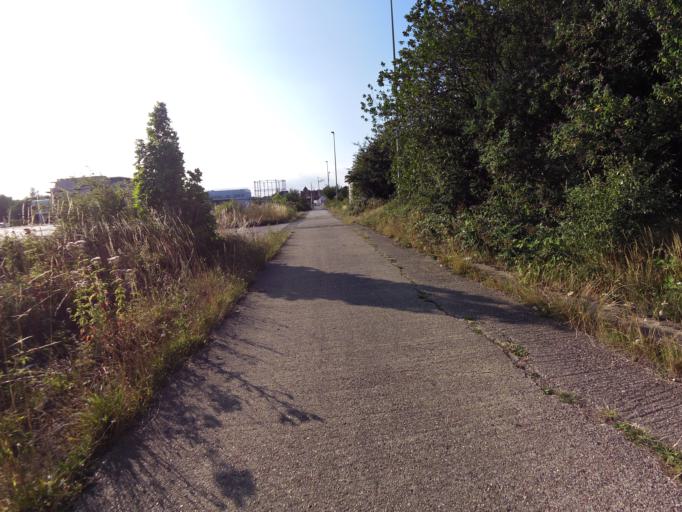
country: GB
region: England
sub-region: Essex
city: Chelmsford
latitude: 51.7298
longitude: 0.4834
